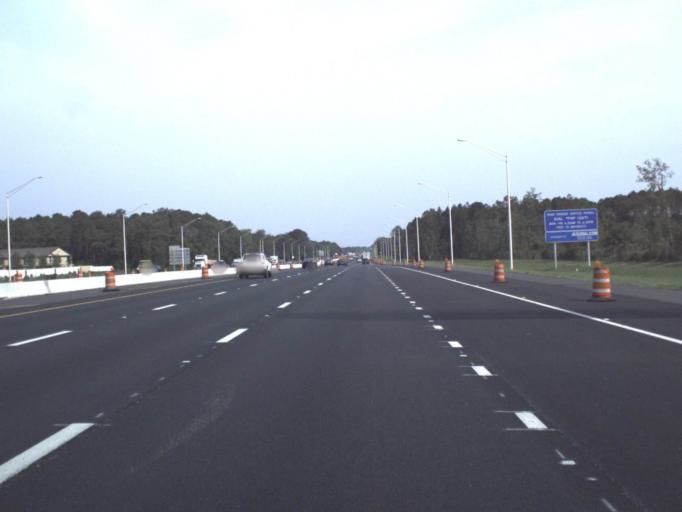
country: US
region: Florida
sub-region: Saint Johns County
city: Fruit Cove
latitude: 30.1222
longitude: -81.5214
